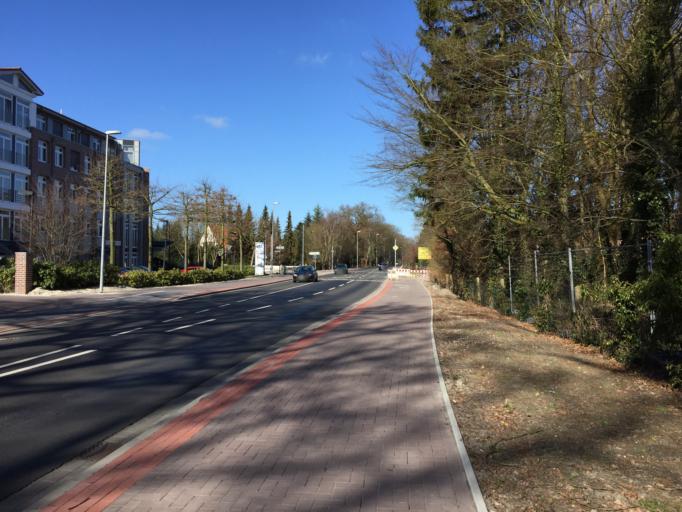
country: DE
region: Lower Saxony
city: Oldenburg
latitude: 53.1746
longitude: 8.2299
